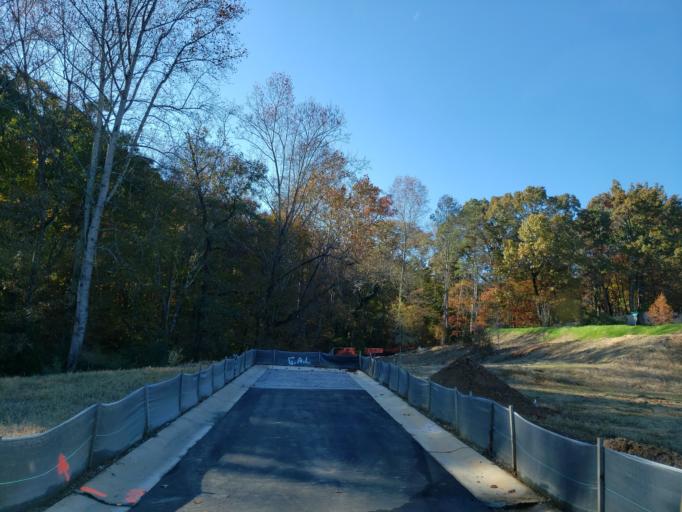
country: US
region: Georgia
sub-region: Fulton County
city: Roswell
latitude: 33.9964
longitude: -84.3526
